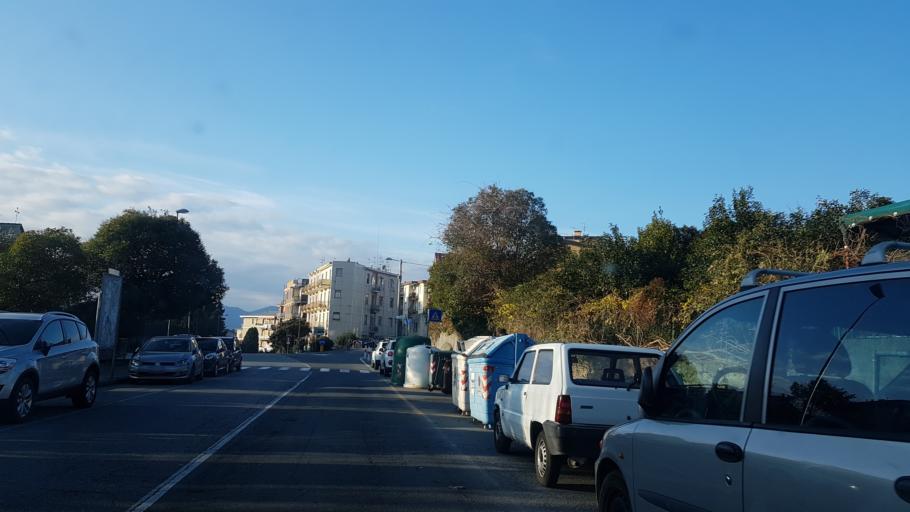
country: IT
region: Liguria
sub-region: Provincia di Savona
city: Savona
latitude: 44.3047
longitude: 8.4607
